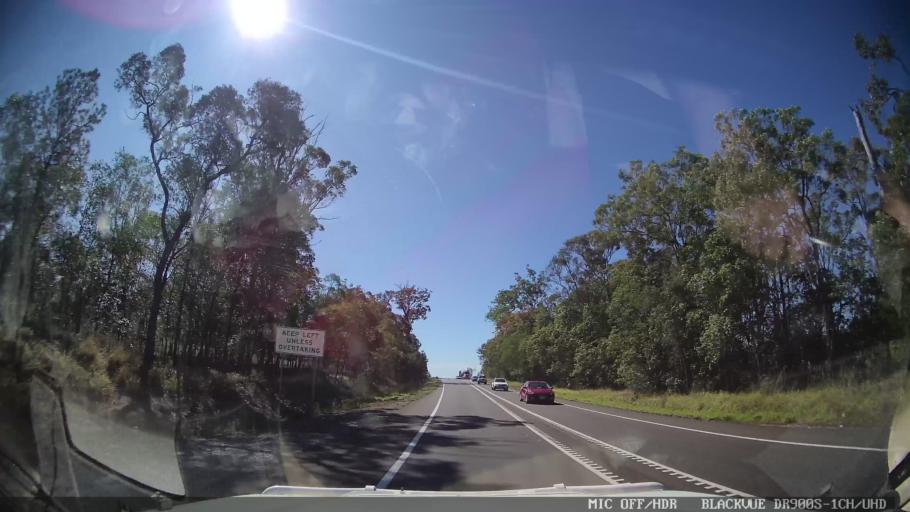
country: AU
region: Queensland
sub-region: Fraser Coast
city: Maryborough
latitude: -25.6490
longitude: 152.6347
